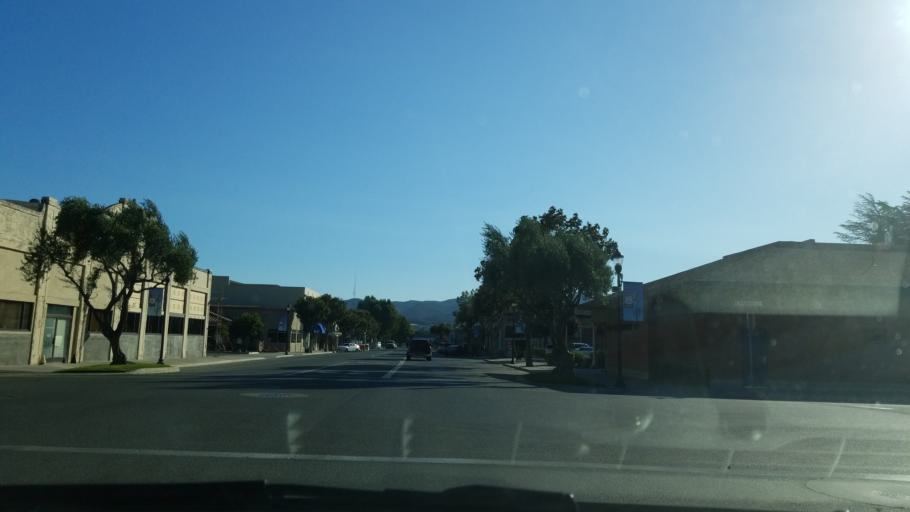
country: US
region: California
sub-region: Monterey County
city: King City
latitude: 36.2123
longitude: -121.1276
